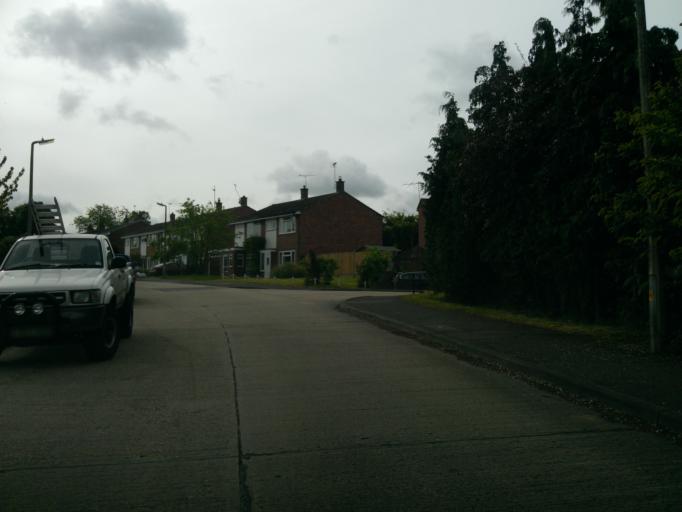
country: GB
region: England
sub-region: Essex
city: Wivenhoe
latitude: 51.8599
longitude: 0.9667
